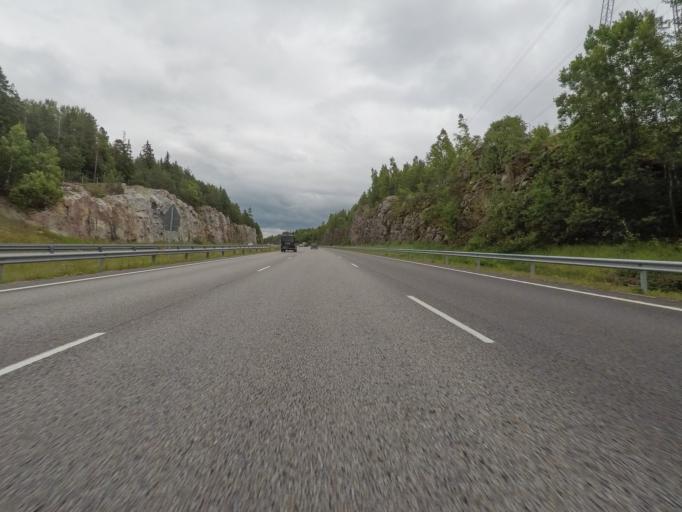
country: FI
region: Varsinais-Suomi
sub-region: Turku
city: Paimio
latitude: 60.4241
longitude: 22.6756
